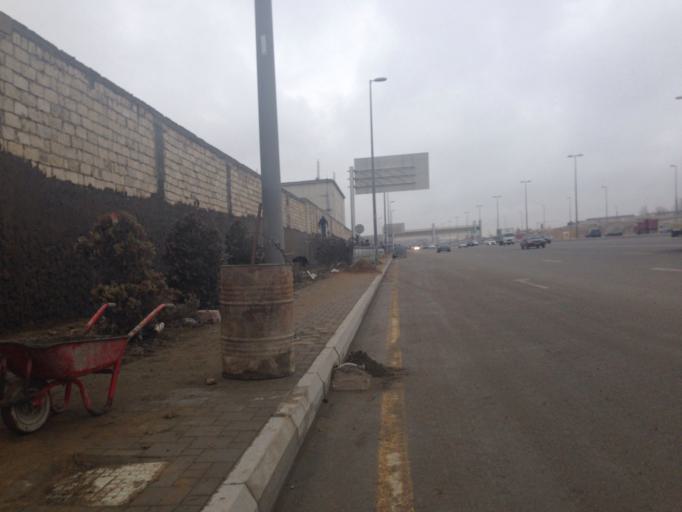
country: AZ
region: Baki
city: Baku
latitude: 40.4226
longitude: 49.8722
